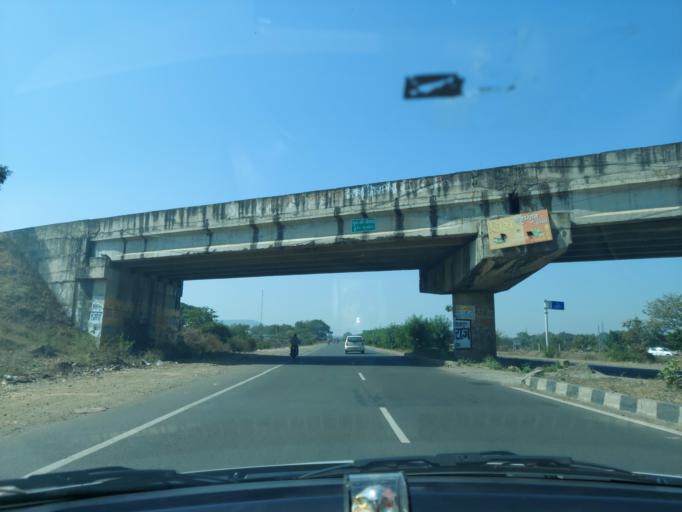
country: IN
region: Madhya Pradesh
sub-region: Indore
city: Manpur
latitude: 22.4280
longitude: 75.6132
